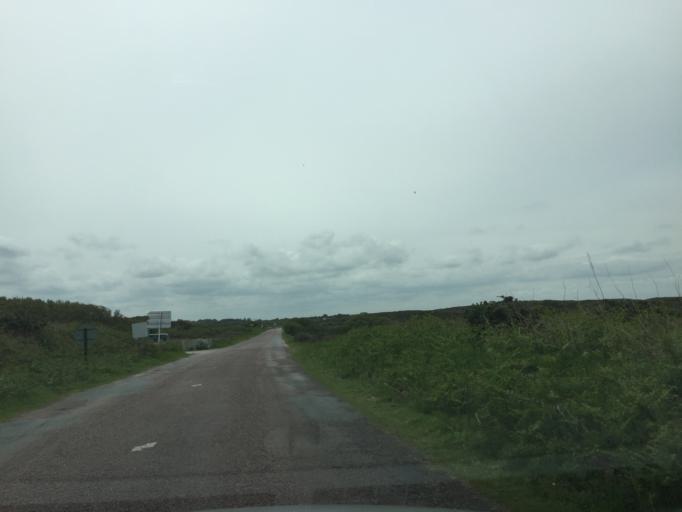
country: FR
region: Brittany
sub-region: Departement des Cotes-d'Armor
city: Saint-Cast-le-Guildo
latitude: 48.6815
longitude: -2.3180
